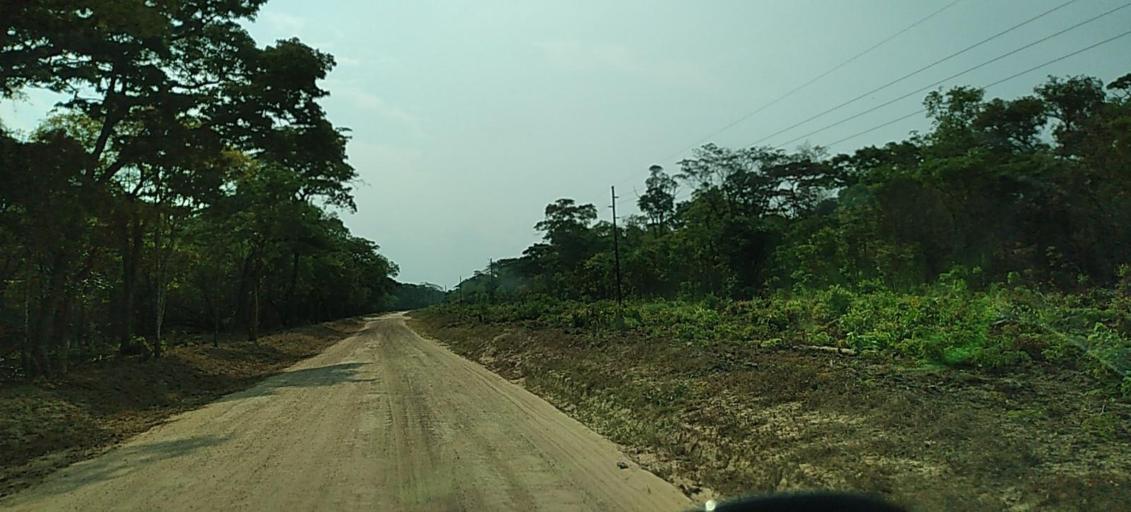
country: ZM
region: North-Western
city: Solwezi
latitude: -12.6815
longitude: 26.3836
